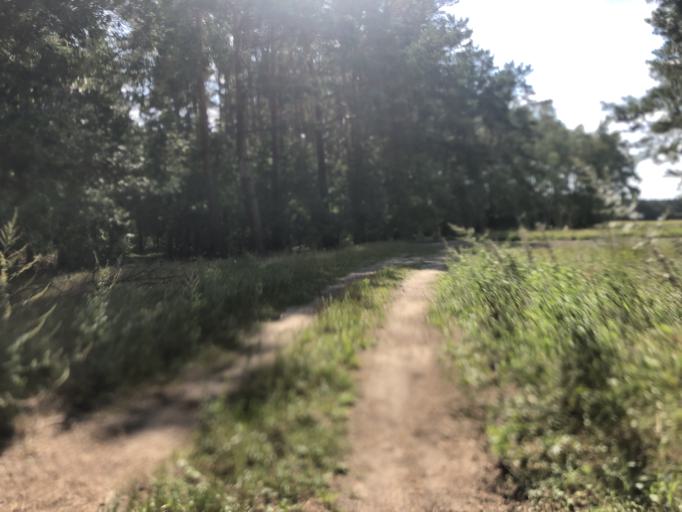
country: DE
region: Brandenburg
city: Mullrose
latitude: 52.2321
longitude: 14.4038
